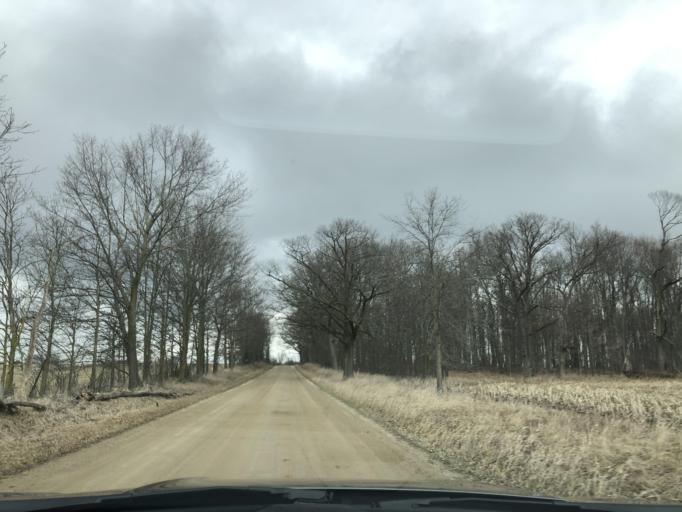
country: US
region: Michigan
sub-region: Clinton County
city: Saint Johns
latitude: 43.0998
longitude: -84.6106
